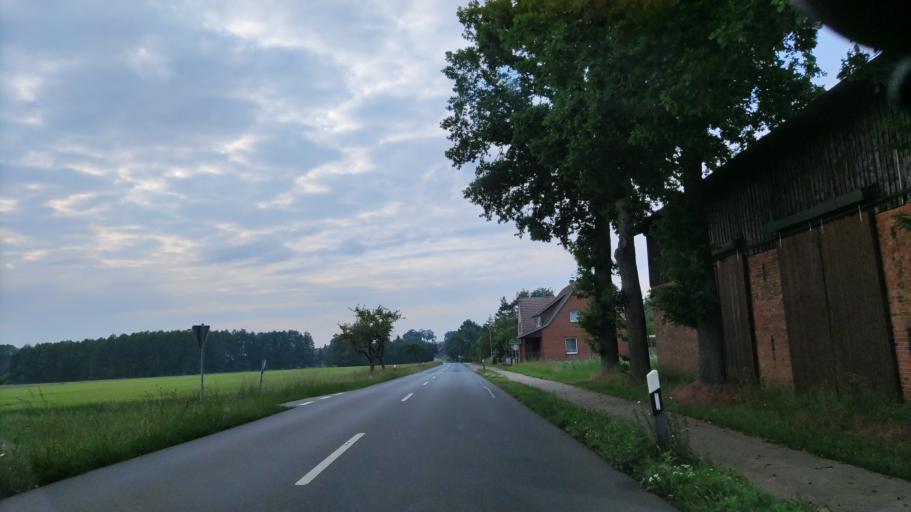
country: DE
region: Lower Saxony
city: Gerdau
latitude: 52.9173
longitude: 10.4176
